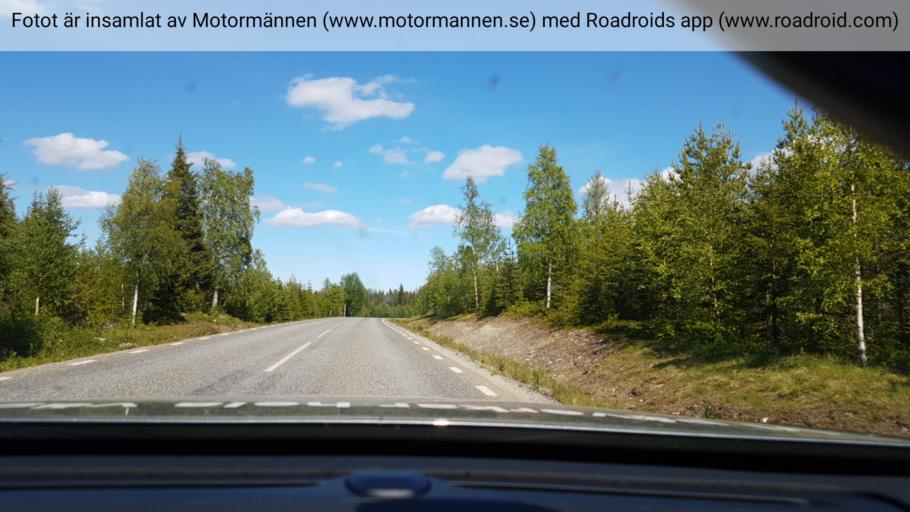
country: SE
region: Vaesterbotten
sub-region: Lycksele Kommun
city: Lycksele
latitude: 64.6233
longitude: 18.3549
